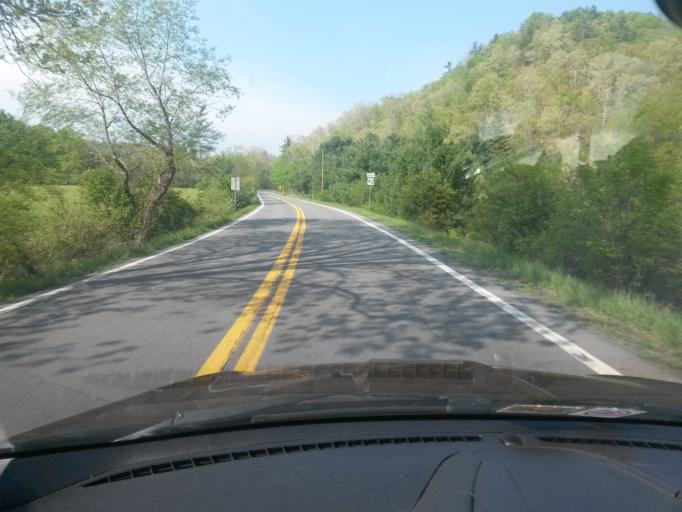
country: US
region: Virginia
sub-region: City of Covington
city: Covington
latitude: 37.9901
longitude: -80.0879
